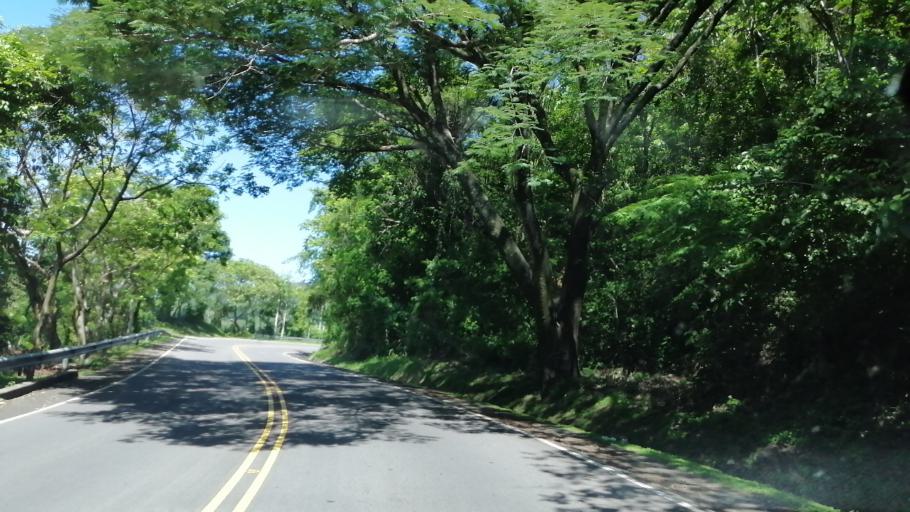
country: SV
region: Morazan
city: Cacaopera
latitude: 13.7993
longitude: -88.1480
